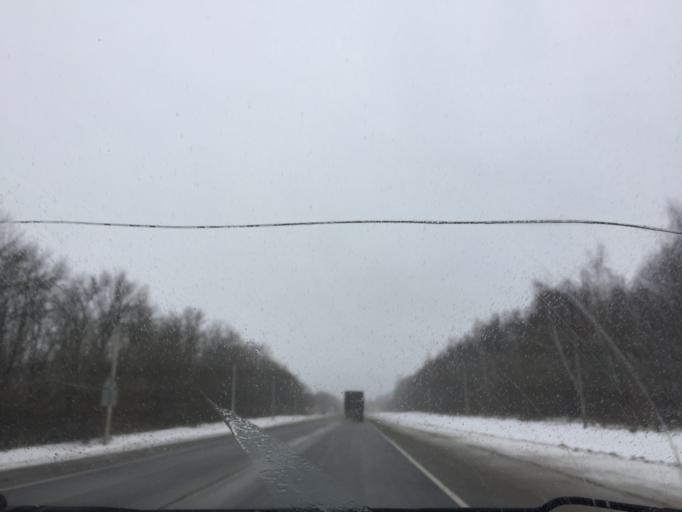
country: RU
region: Tula
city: Plavsk
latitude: 53.7496
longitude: 37.3265
